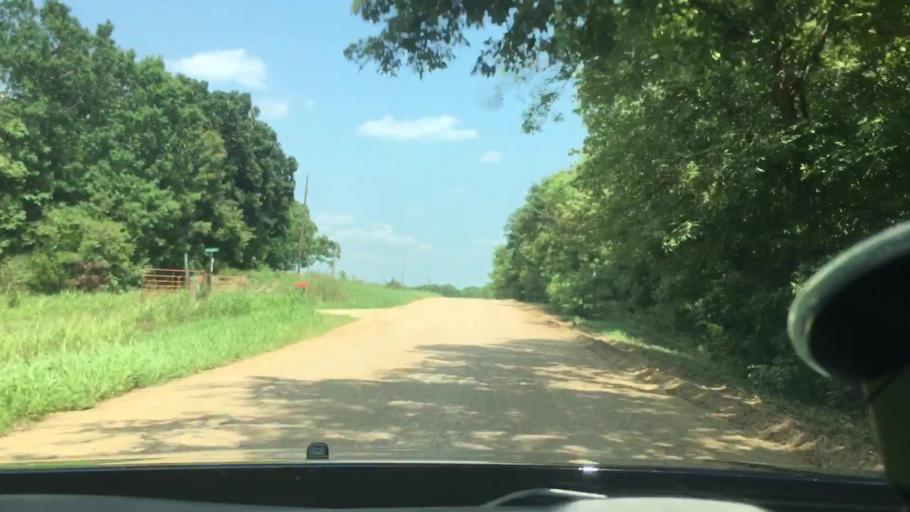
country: US
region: Oklahoma
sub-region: Coal County
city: Coalgate
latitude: 34.4310
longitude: -96.4533
